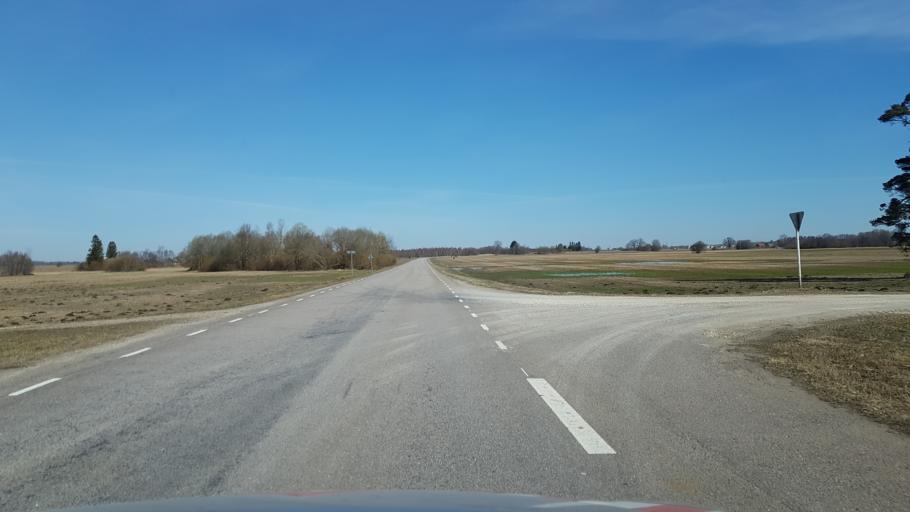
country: EE
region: Laeaene-Virumaa
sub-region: Vaeike-Maarja vald
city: Vaike-Maarja
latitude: 59.2122
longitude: 26.3330
